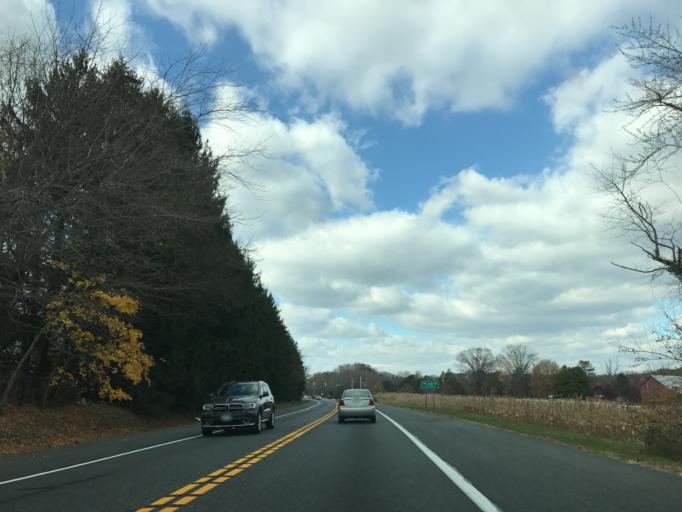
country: US
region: Maryland
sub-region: Harford County
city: Pleasant Hills
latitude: 39.4744
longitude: -76.3776
